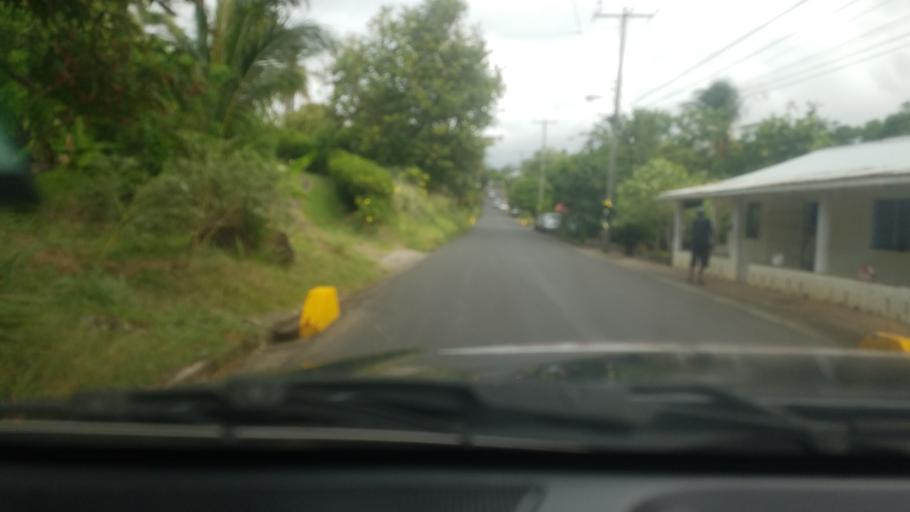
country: LC
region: Micoud Quarter
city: Micoud
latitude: 13.7976
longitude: -60.9167
